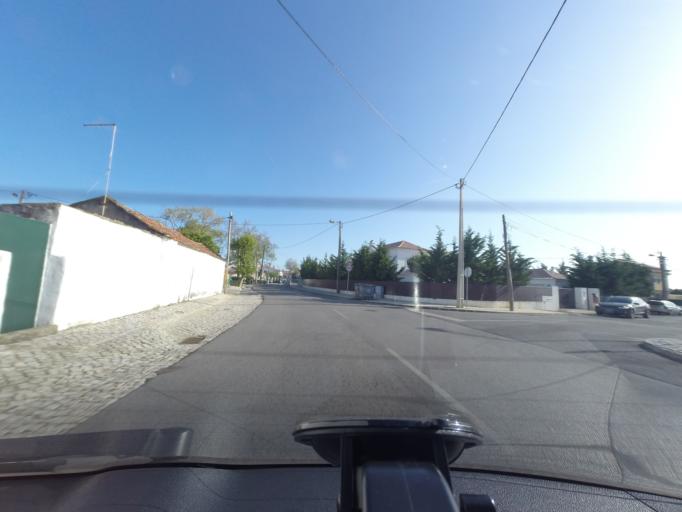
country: PT
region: Lisbon
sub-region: Cascais
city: Alcabideche
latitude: 38.7332
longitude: -9.4397
